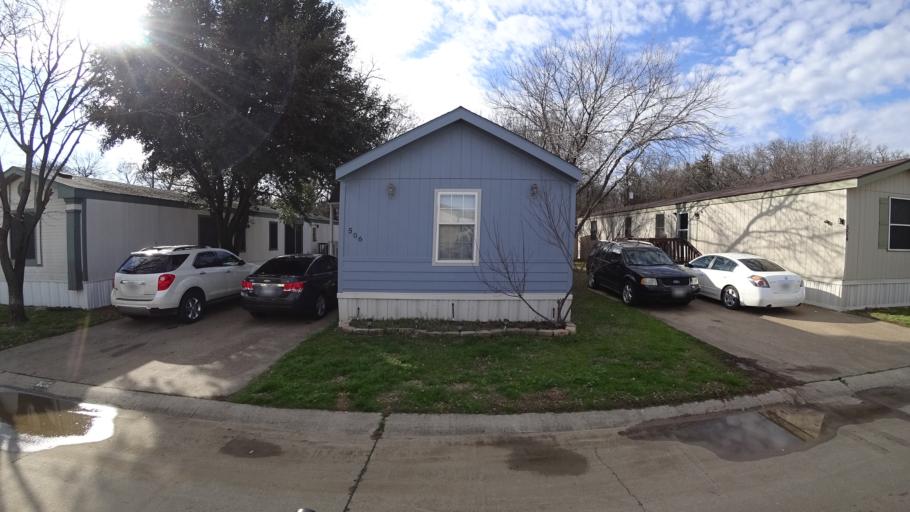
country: US
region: Texas
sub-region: Dallas County
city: Coppell
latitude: 32.9958
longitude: -97.0180
